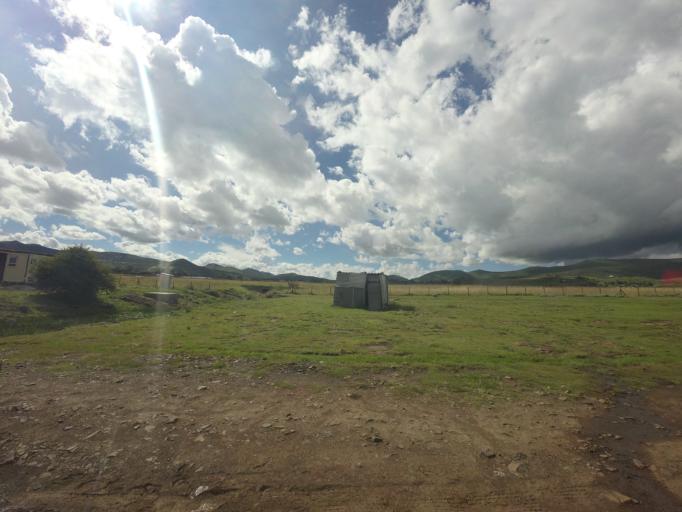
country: LS
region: Maseru
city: Nako
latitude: -29.8410
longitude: 28.0560
